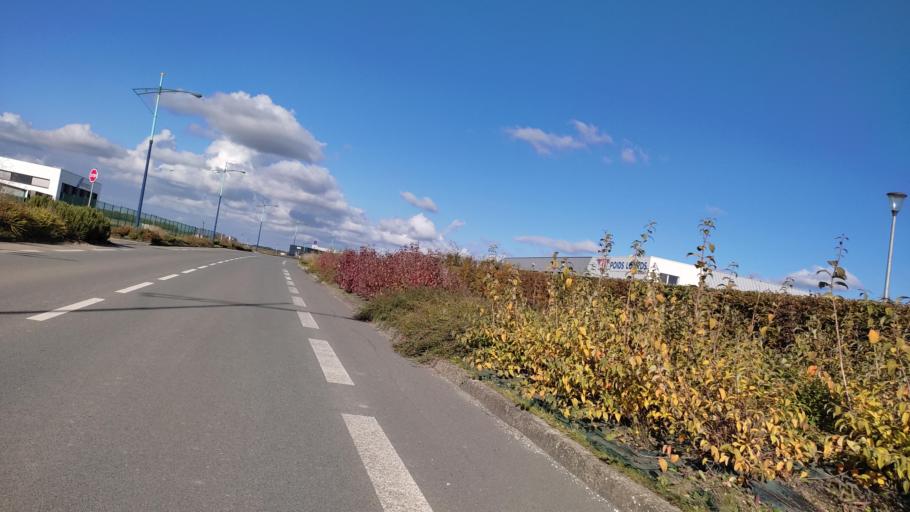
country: FR
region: Nord-Pas-de-Calais
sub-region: Departement du Pas-de-Calais
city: Saint-Laurent-Blangy
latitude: 50.3175
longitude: 2.8219
